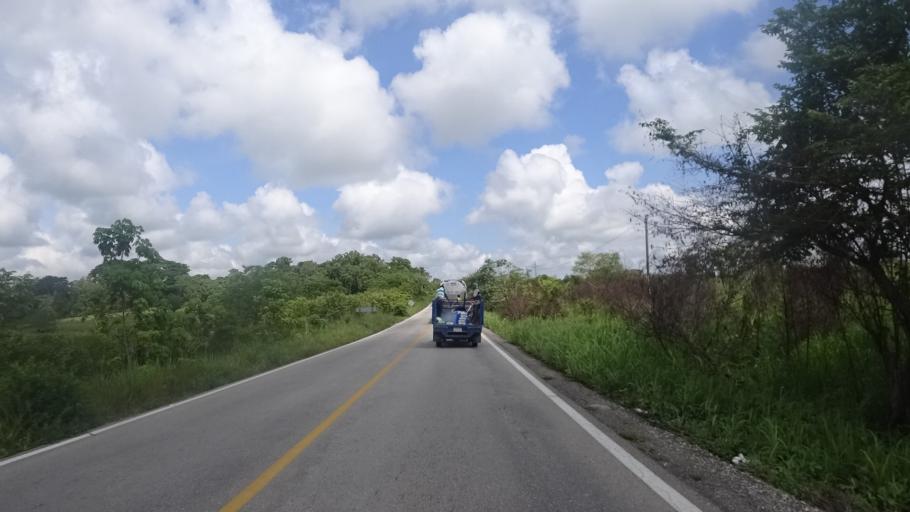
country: MX
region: Chiapas
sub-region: Catazaja
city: Catazaja
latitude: 17.6376
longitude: -92.0283
